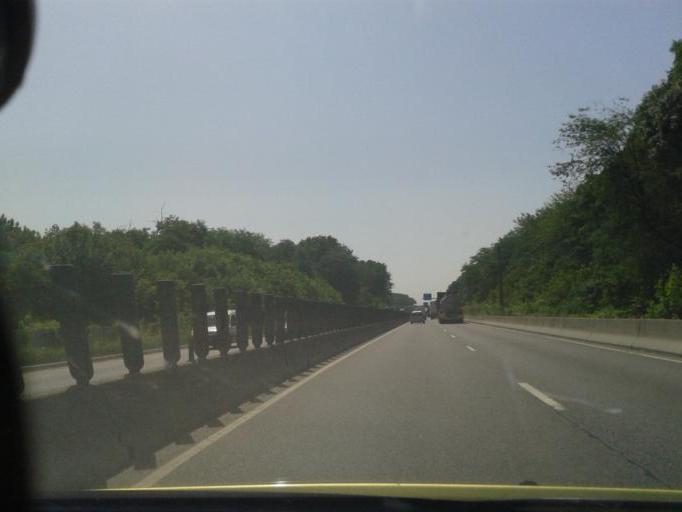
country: RO
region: Ilfov
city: Stefanestii de Jos
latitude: 44.5166
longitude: 26.1827
